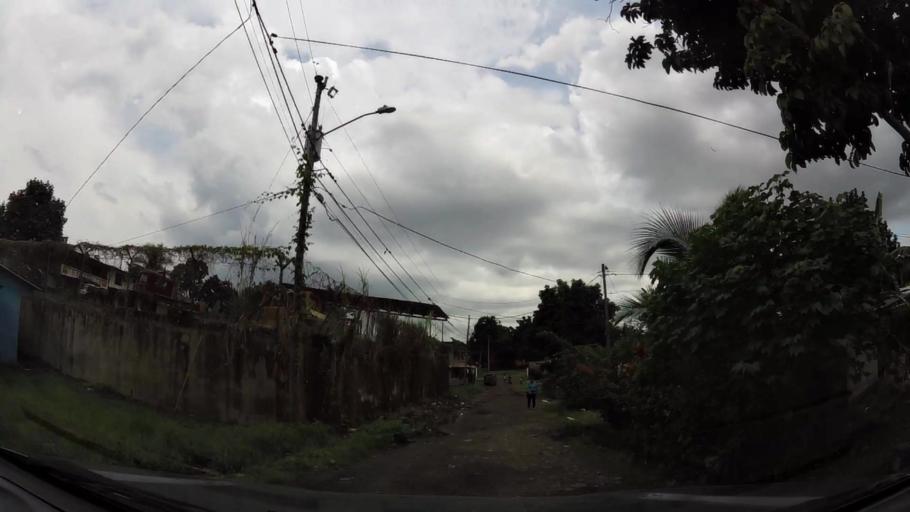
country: PA
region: Panama
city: Cabra Numero Uno
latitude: 9.1101
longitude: -79.3224
